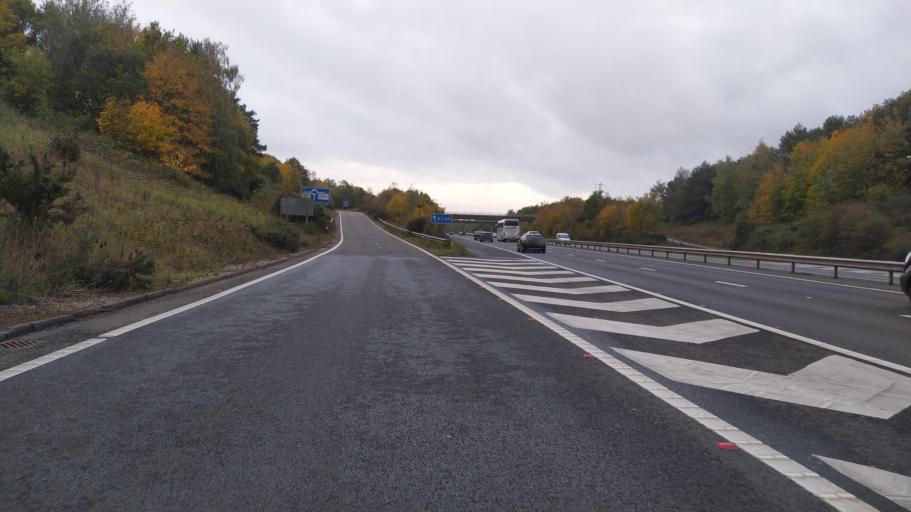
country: GB
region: England
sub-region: Hampshire
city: Cowplain
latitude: 50.9096
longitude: -0.9989
